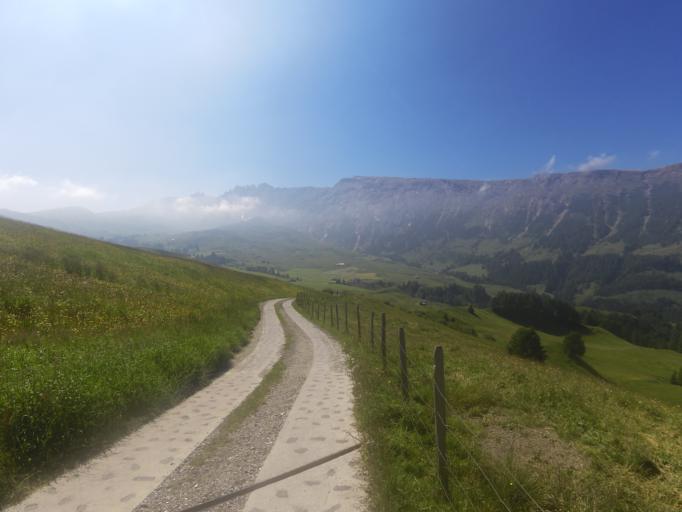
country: IT
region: Trentino-Alto Adige
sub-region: Bolzano
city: Siusi
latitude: 46.5260
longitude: 11.6057
